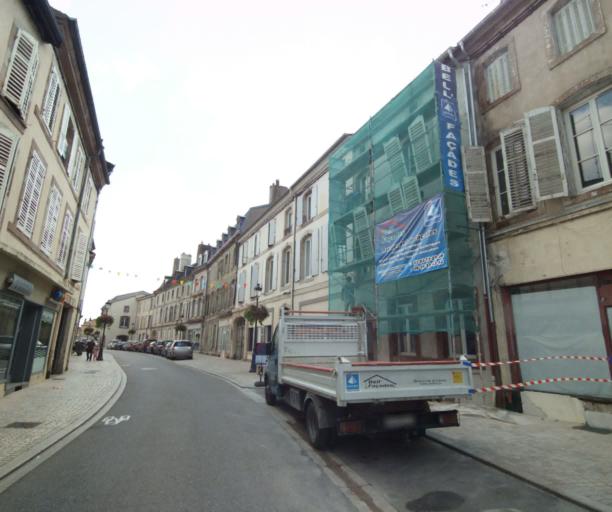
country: FR
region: Lorraine
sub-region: Departement de Meurthe-et-Moselle
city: Luneville
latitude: 48.5924
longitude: 6.4905
